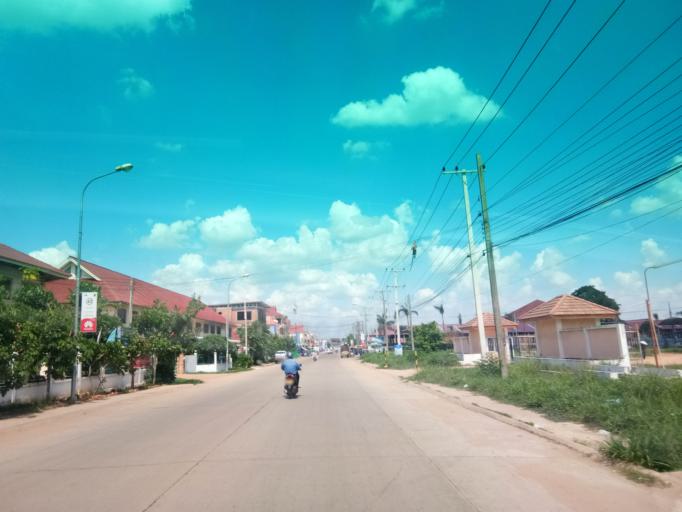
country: LA
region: Savannahkhet
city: Savannakhet
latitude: 16.5792
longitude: 104.7480
